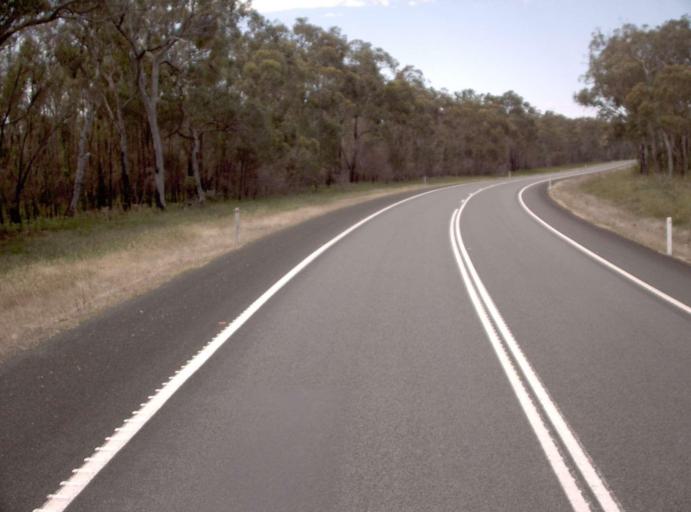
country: AU
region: New South Wales
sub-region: Bega Valley
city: Eden
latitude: -37.5173
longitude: 149.4979
